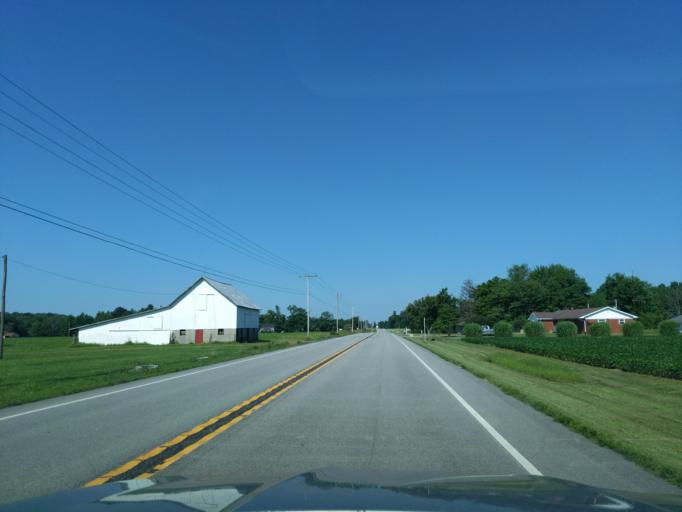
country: US
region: Indiana
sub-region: Ripley County
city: Osgood
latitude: 39.0749
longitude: -85.3113
